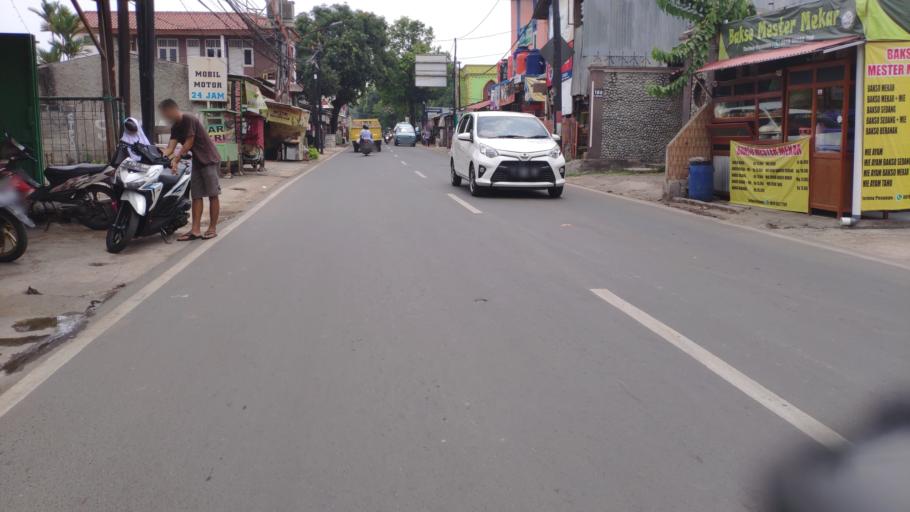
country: ID
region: West Java
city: Depok
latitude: -6.3504
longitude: 106.8017
